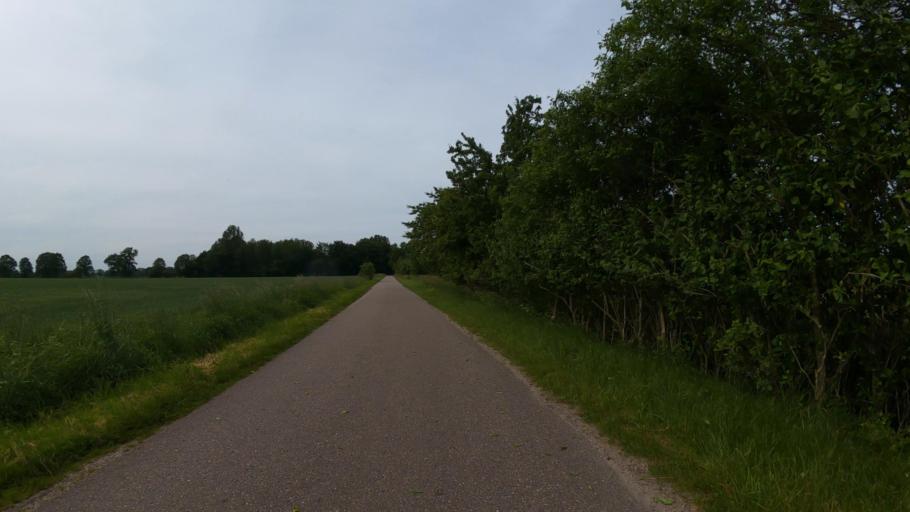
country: DE
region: Schleswig-Holstein
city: Hartenholm
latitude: 53.8728
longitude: 10.0807
